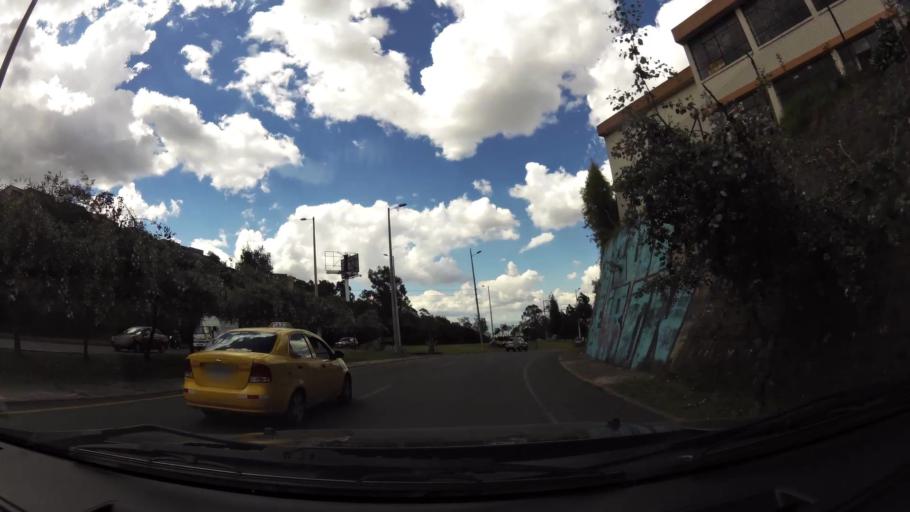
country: EC
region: Pichincha
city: Quito
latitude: -0.1832
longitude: -78.5088
